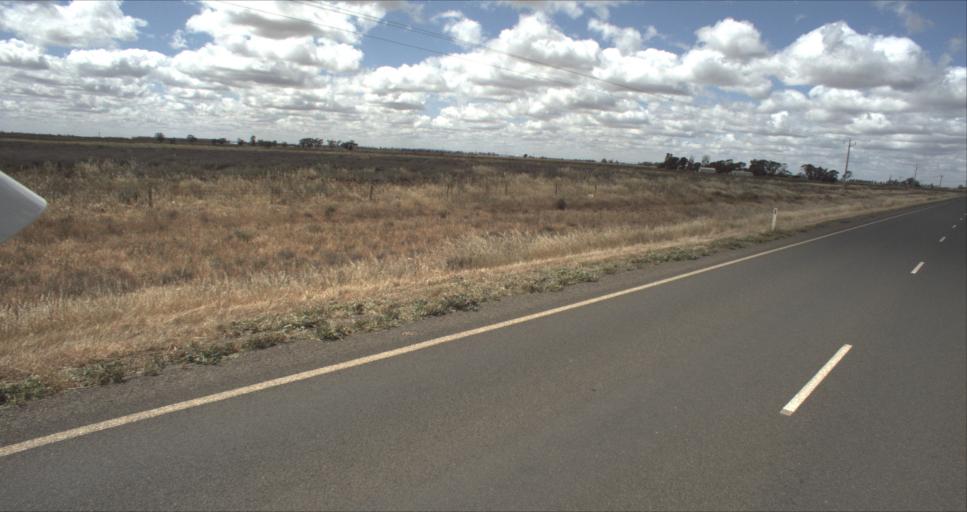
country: AU
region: New South Wales
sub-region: Murrumbidgee Shire
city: Darlington Point
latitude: -34.4910
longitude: 146.1647
